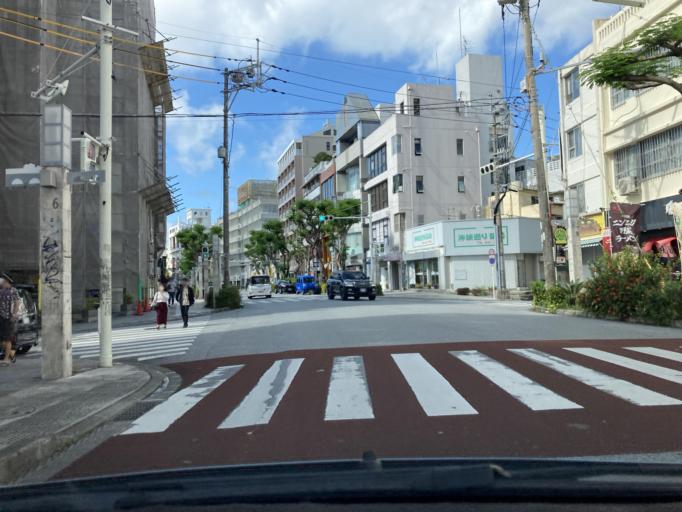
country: JP
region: Okinawa
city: Naha-shi
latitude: 26.2177
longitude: 127.6873
